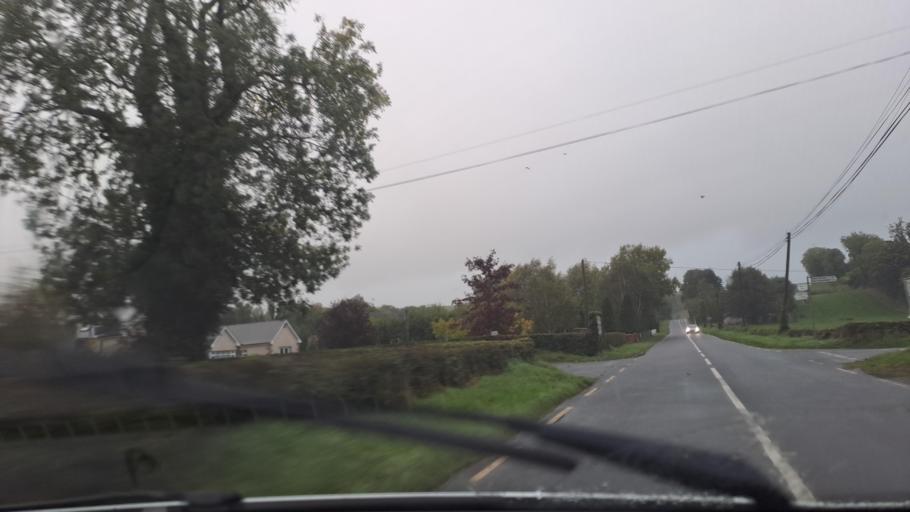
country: IE
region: Ulster
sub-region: County Monaghan
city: Carrickmacross
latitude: 53.9879
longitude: -6.6958
